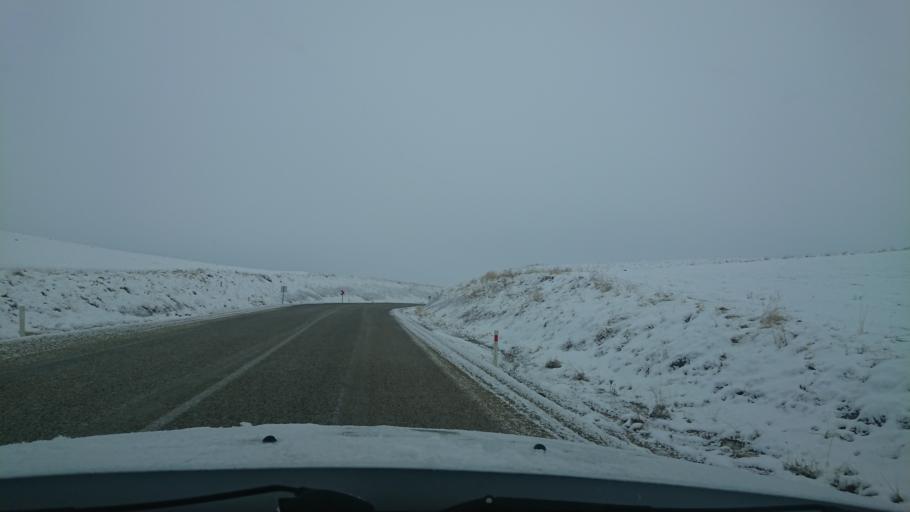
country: TR
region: Aksaray
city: Agacoren
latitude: 38.7704
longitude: 33.8693
